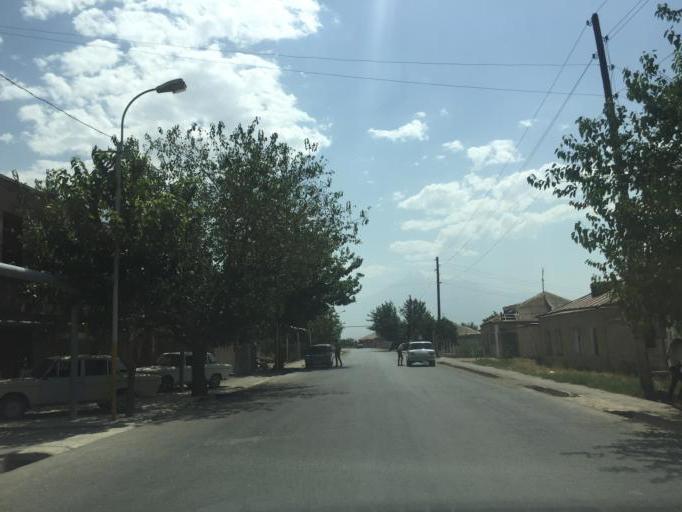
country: AM
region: Ararat
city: Shahumyan
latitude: 39.9013
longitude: 44.6005
